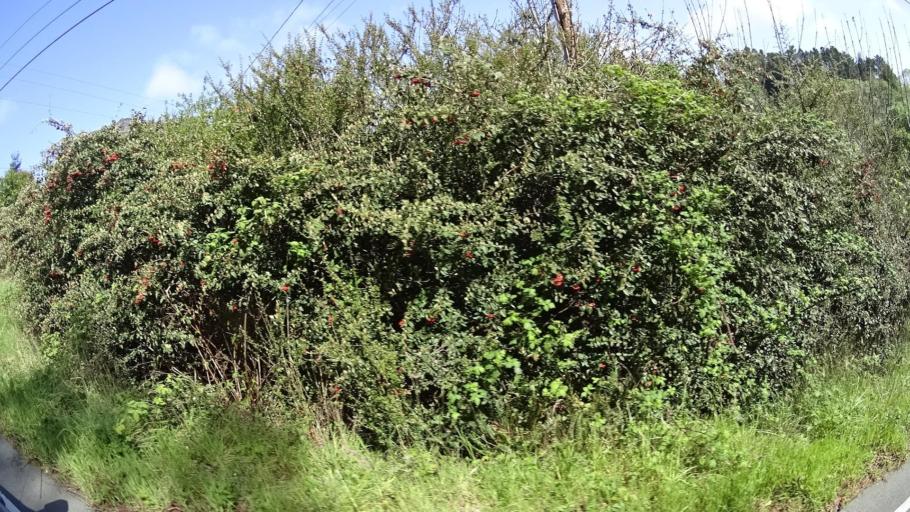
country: US
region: California
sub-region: Humboldt County
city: Bayview
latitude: 40.7697
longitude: -124.1771
